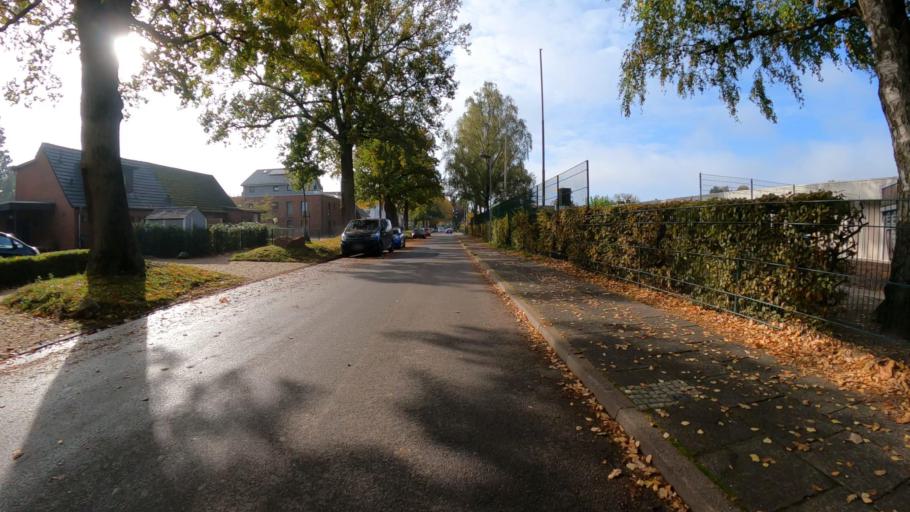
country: DE
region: Schleswig-Holstein
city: Ahrensburg
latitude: 53.6422
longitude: 10.2176
